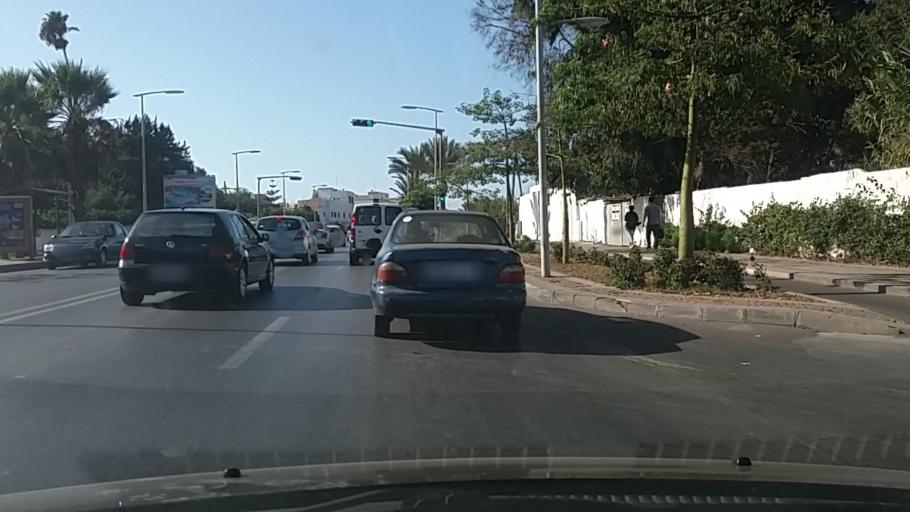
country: MA
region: Rabat-Sale-Zemmour-Zaer
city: Sale
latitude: 34.0432
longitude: -6.8173
